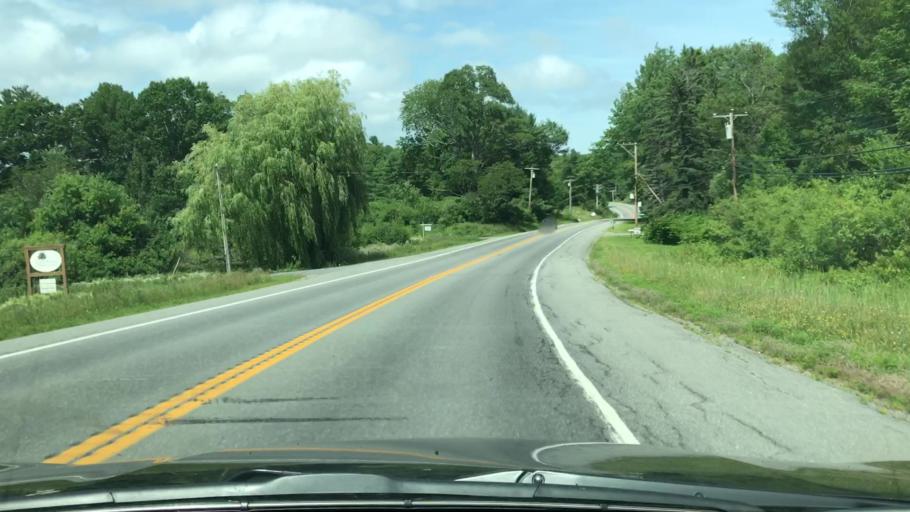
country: US
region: Maine
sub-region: Waldo County
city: Belfast
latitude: 44.3921
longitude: -68.9906
